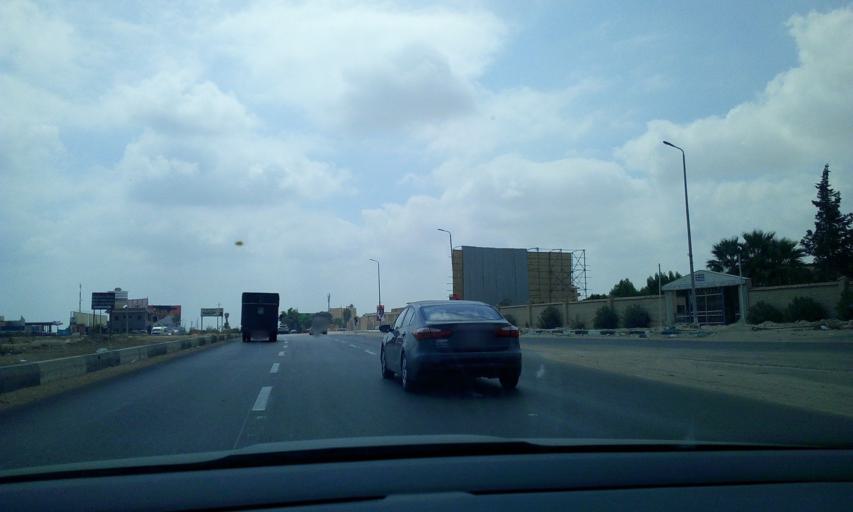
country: EG
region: Muhafazat Matruh
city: Al `Alamayn
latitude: 30.8364
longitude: 28.9577
